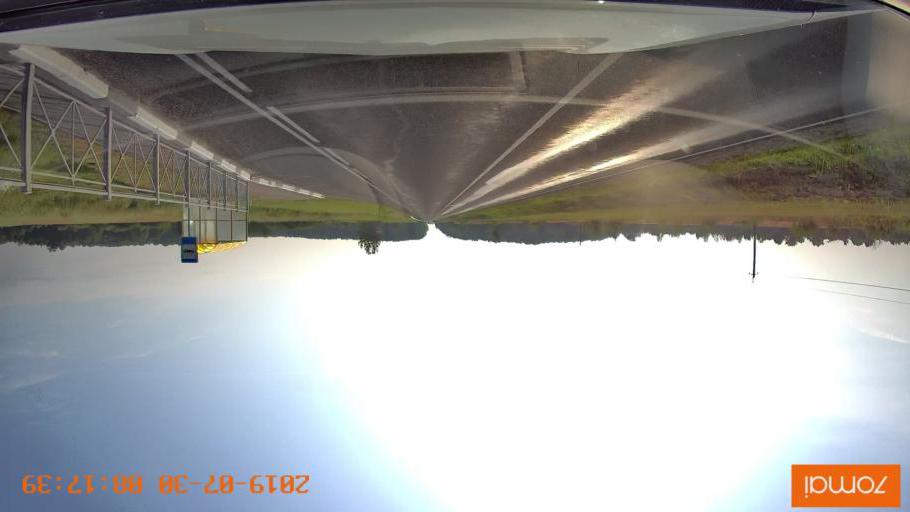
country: RU
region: Kaliningrad
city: Zheleznodorozhnyy
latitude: 54.6355
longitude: 21.4431
